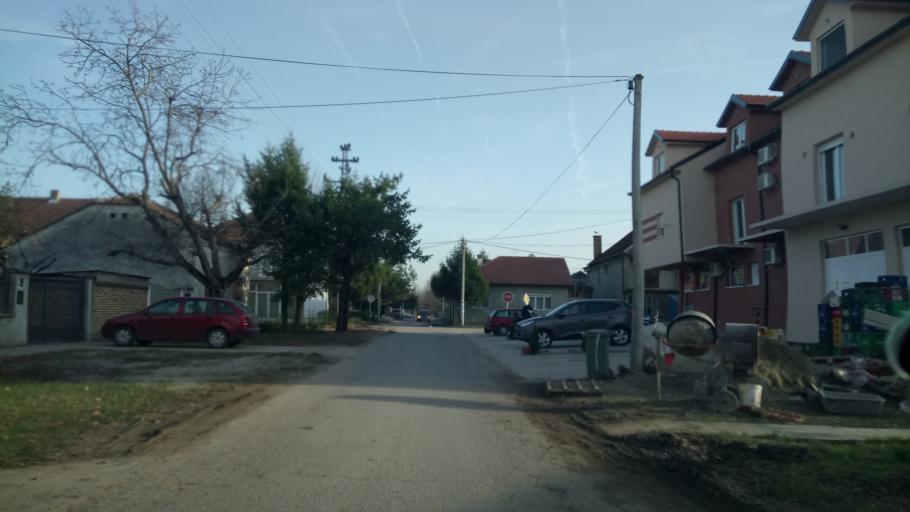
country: RS
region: Autonomna Pokrajina Vojvodina
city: Nova Pazova
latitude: 44.9465
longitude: 20.2306
